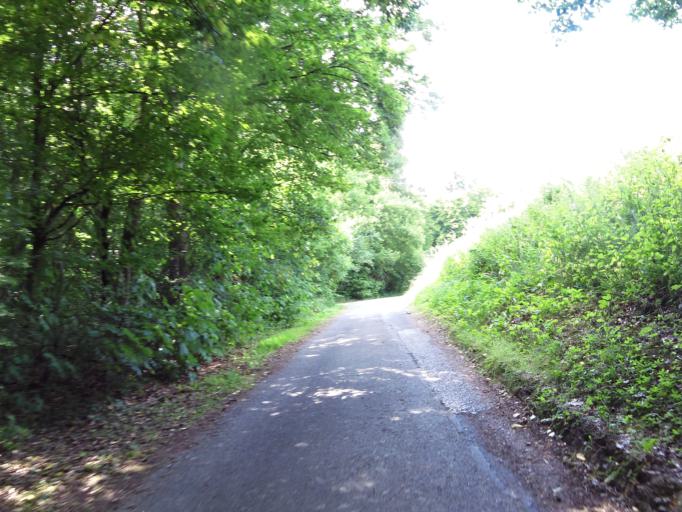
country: DE
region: Bavaria
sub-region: Regierungsbezirk Unterfranken
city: Gadheim
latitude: 49.8267
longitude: 9.9179
